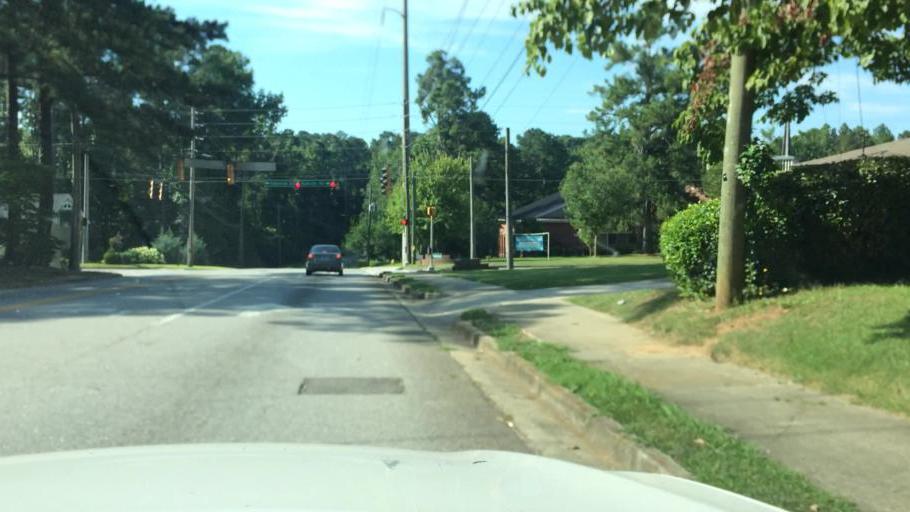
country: US
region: Georgia
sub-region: Columbia County
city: Martinez
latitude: 33.4950
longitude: -82.0384
